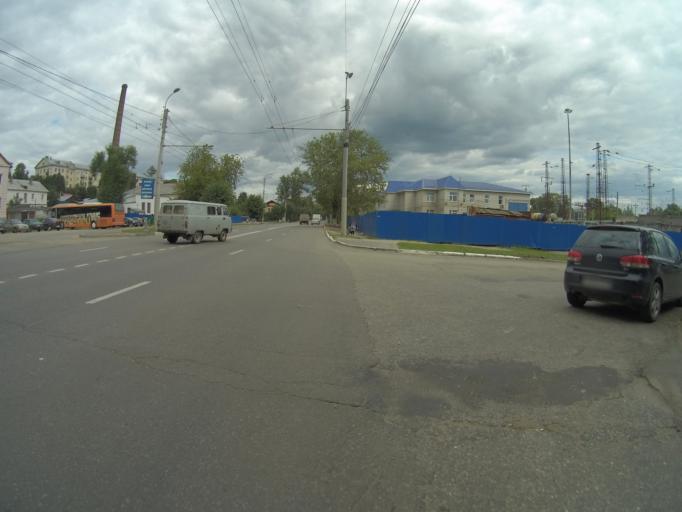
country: RU
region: Vladimir
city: Kommunar
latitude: 56.1334
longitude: 40.4263
